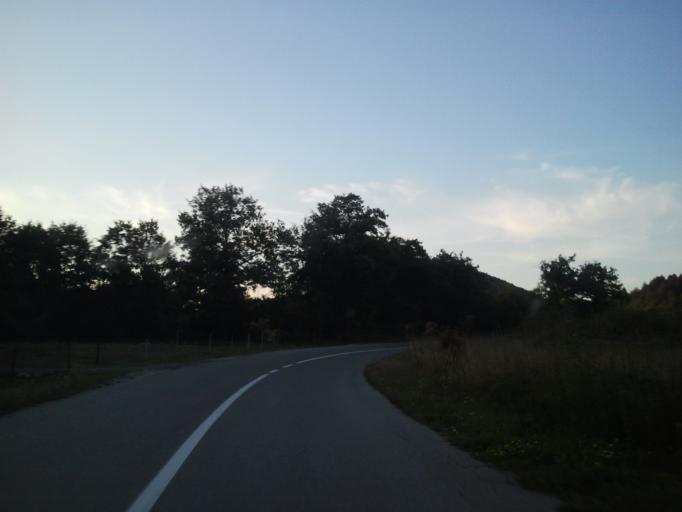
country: HR
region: Zadarska
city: Obrovac
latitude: 44.4221
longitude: 15.6603
